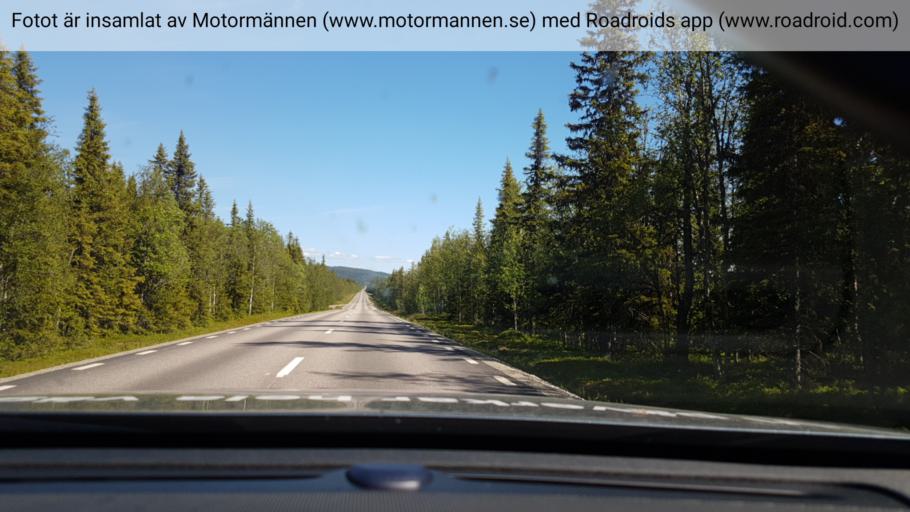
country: SE
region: Vaesterbotten
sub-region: Asele Kommun
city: Insjon
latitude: 64.7275
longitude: 17.5620
